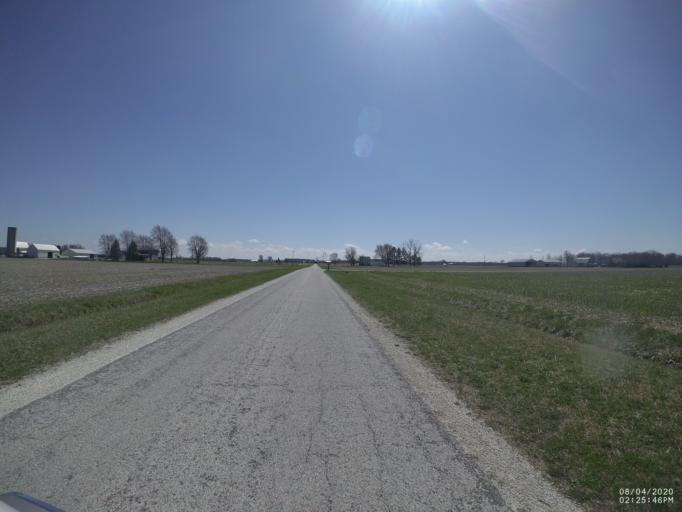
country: US
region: Ohio
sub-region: Sandusky County
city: Gibsonburg
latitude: 41.2939
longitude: -83.2596
